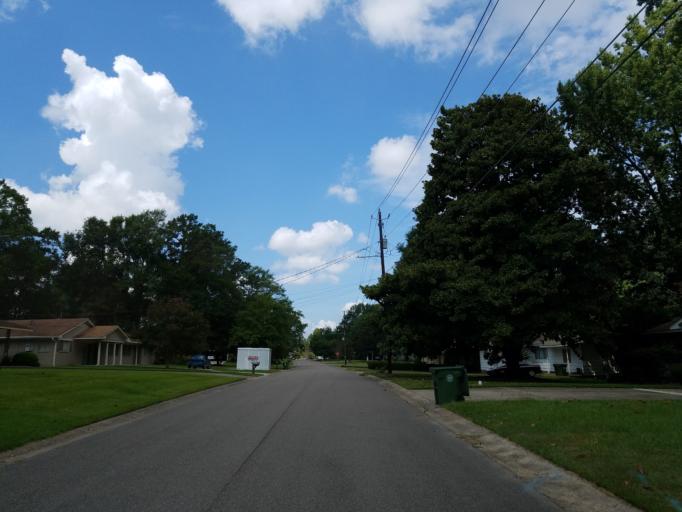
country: US
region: Mississippi
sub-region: Lamar County
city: West Hattiesburg
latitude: 31.3122
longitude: -89.3332
